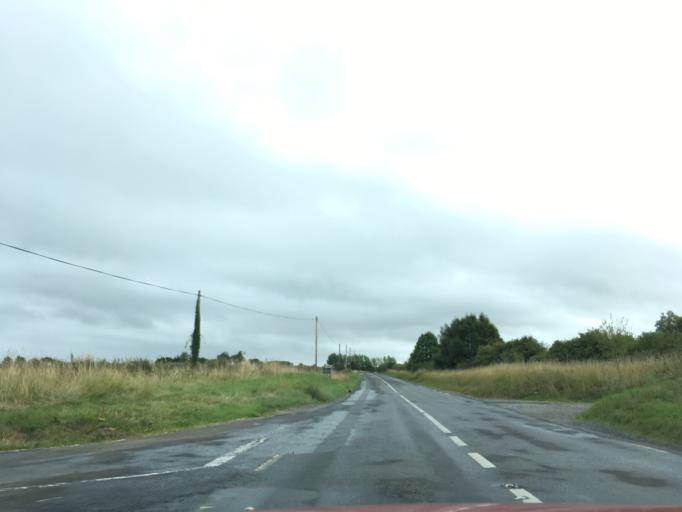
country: IE
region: Munster
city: Cashel
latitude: 52.4483
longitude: -7.8095
